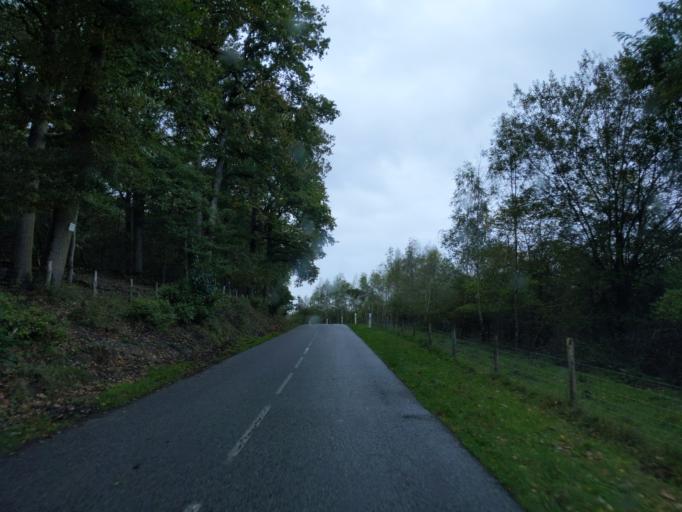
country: FR
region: Ile-de-France
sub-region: Departement des Yvelines
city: Bullion
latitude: 48.6307
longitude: 1.9631
